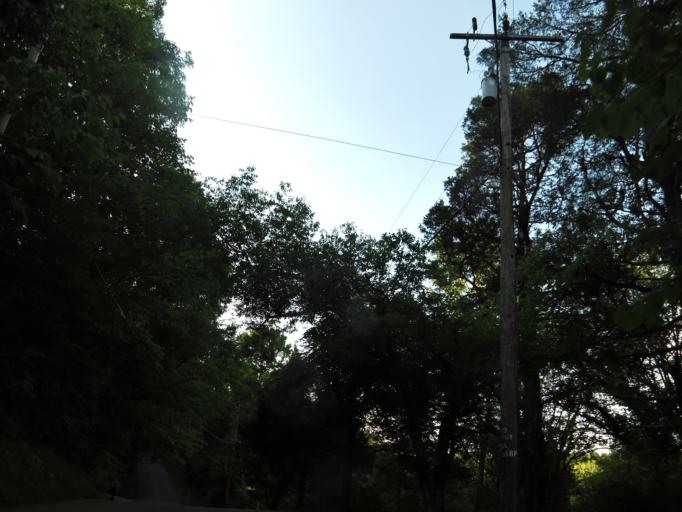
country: US
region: Tennessee
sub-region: Knox County
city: Knoxville
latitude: 35.9098
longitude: -83.9098
